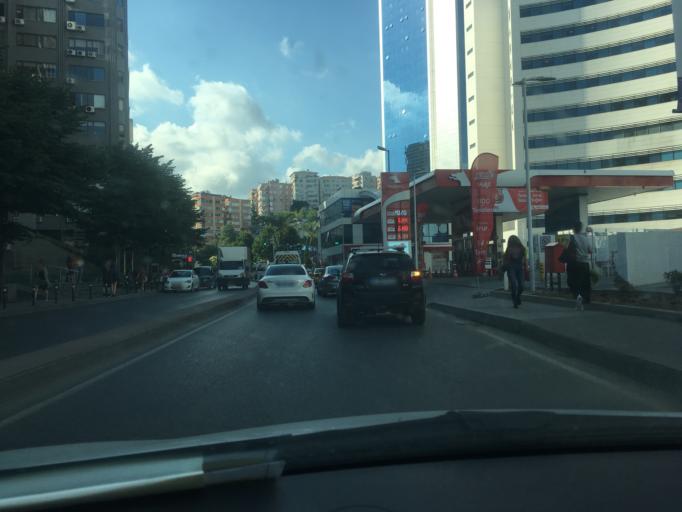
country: TR
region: Istanbul
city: Sisli
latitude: 41.0547
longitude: 28.9993
